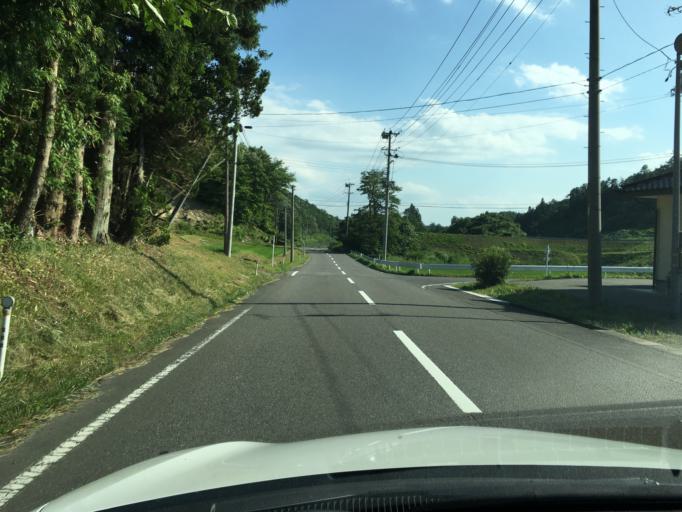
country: JP
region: Fukushima
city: Ishikawa
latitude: 37.2206
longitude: 140.5446
